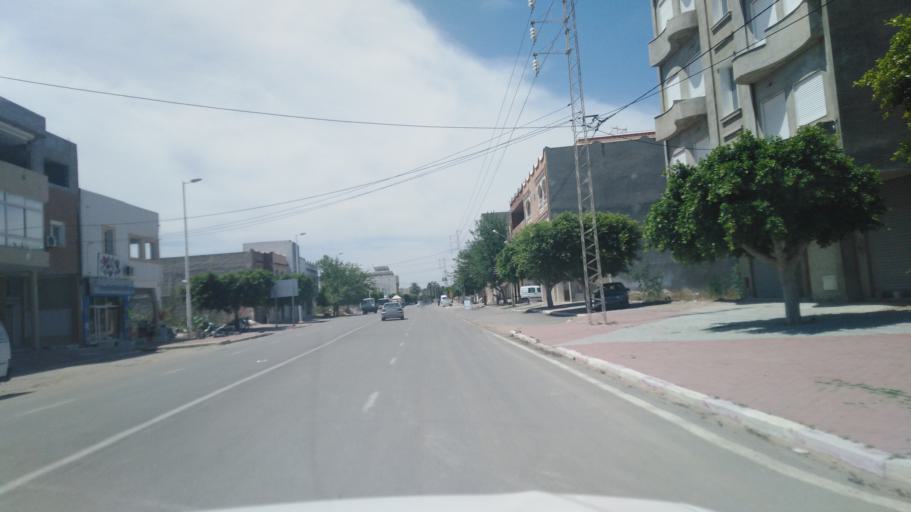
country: TN
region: Al Mahdiyah
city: Ksour Essaf
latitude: 35.4294
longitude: 11.0018
